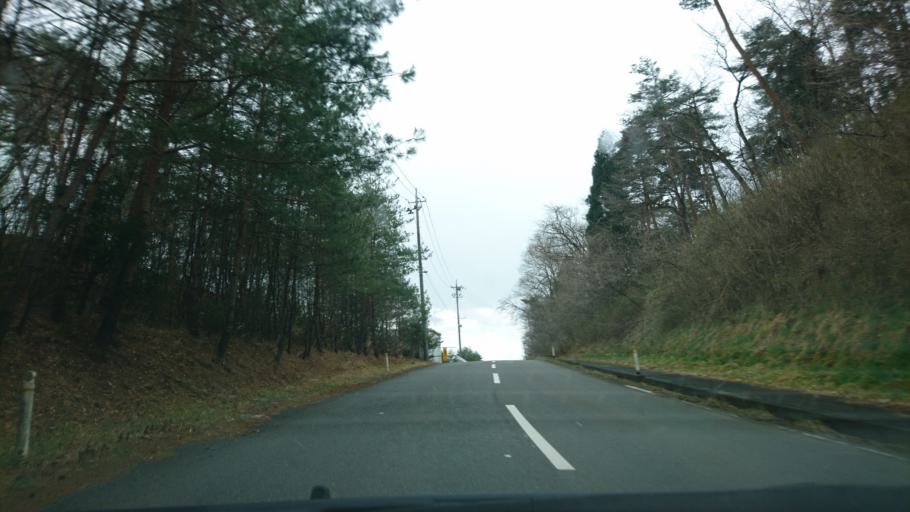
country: JP
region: Iwate
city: Ichinoseki
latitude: 38.8310
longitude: 141.1723
